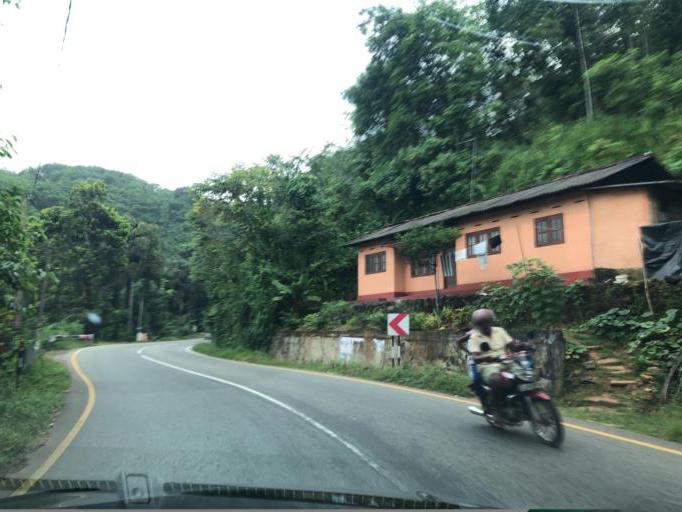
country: LK
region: Western
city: Horana South
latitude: 6.6799
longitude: 80.1275
